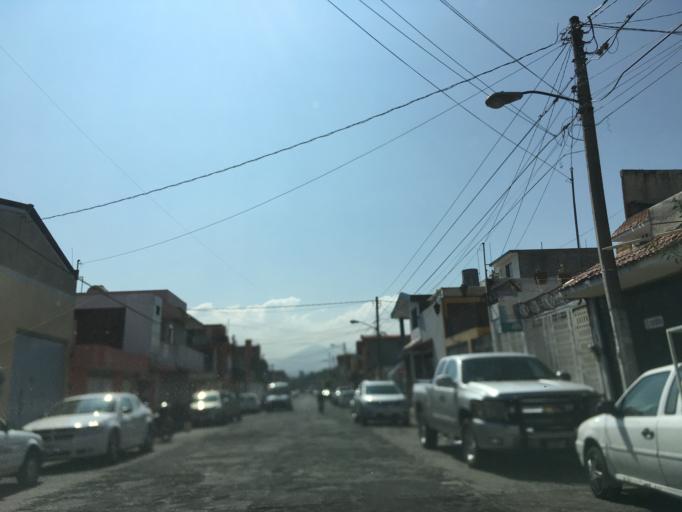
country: MX
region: Michoacan
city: Morelia
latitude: 19.7009
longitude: -101.2050
